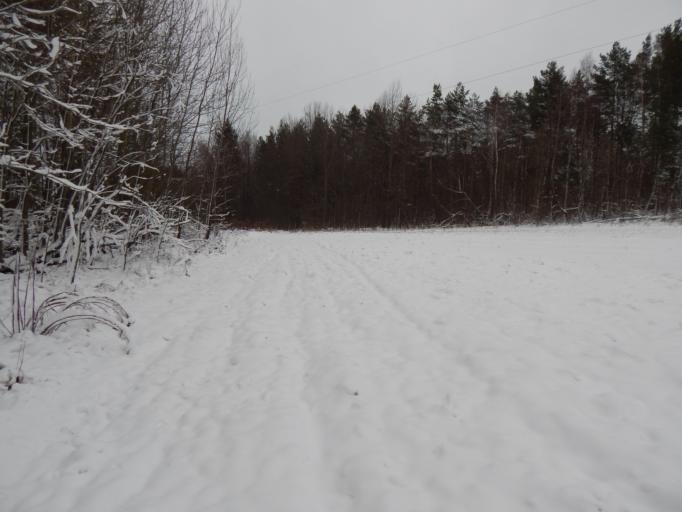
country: BY
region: Minsk
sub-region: Minski Rayon
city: Krasnaye
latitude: 54.1312
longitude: 27.0868
